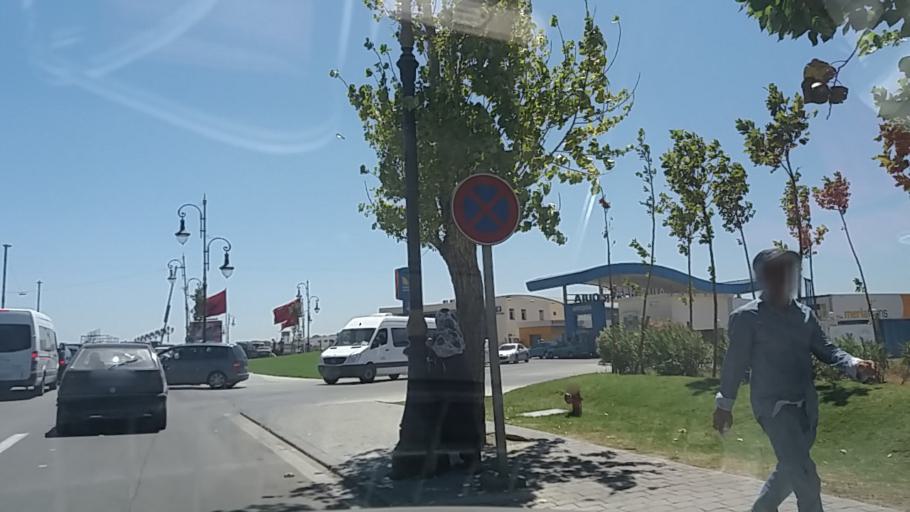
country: MA
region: Tanger-Tetouan
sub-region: Tanger-Assilah
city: Tangier
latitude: 35.7536
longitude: -5.7902
